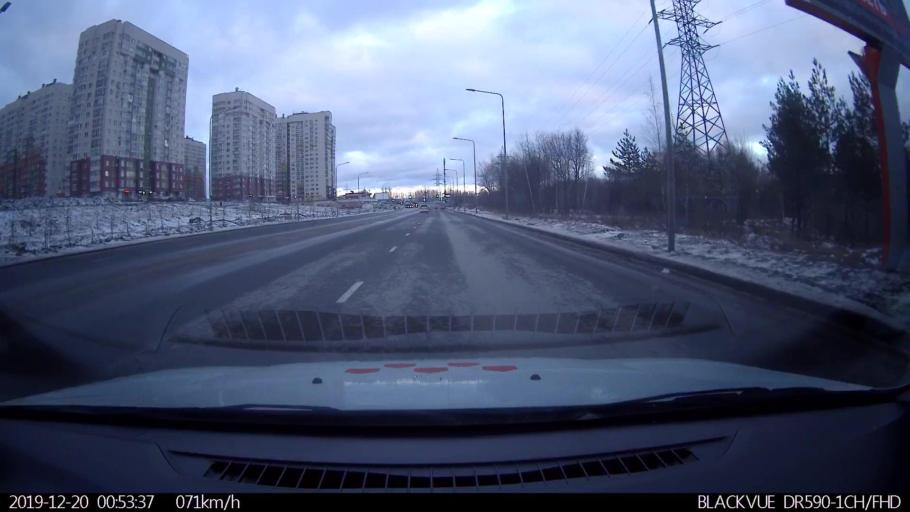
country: RU
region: Nizjnij Novgorod
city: Nizhniy Novgorod
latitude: 56.2591
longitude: 44.0170
